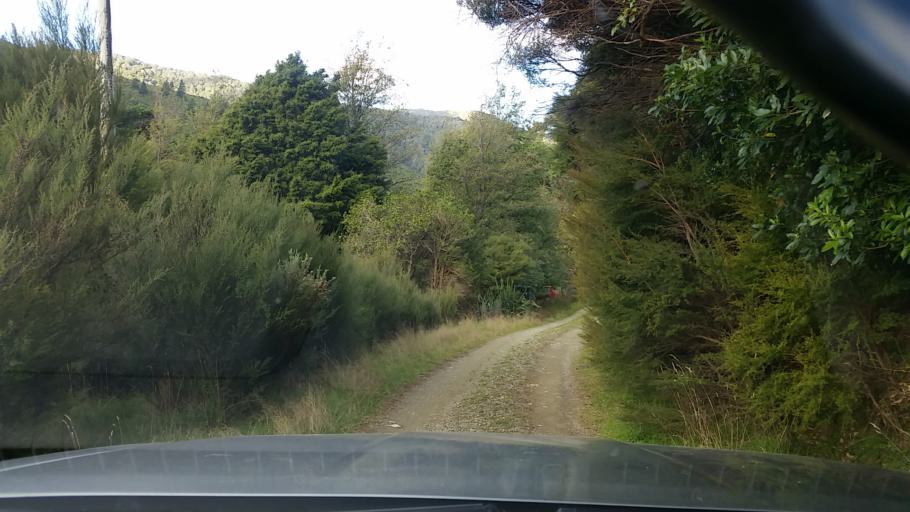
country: NZ
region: Marlborough
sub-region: Marlborough District
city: Picton
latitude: -41.0606
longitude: 174.1146
